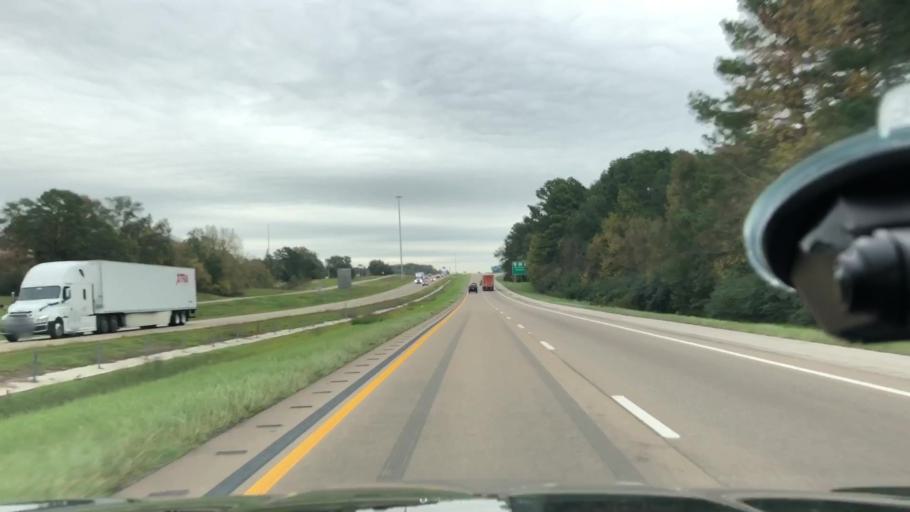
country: US
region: Texas
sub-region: Titus County
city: Mount Pleasant
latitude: 33.1667
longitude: -95.0091
